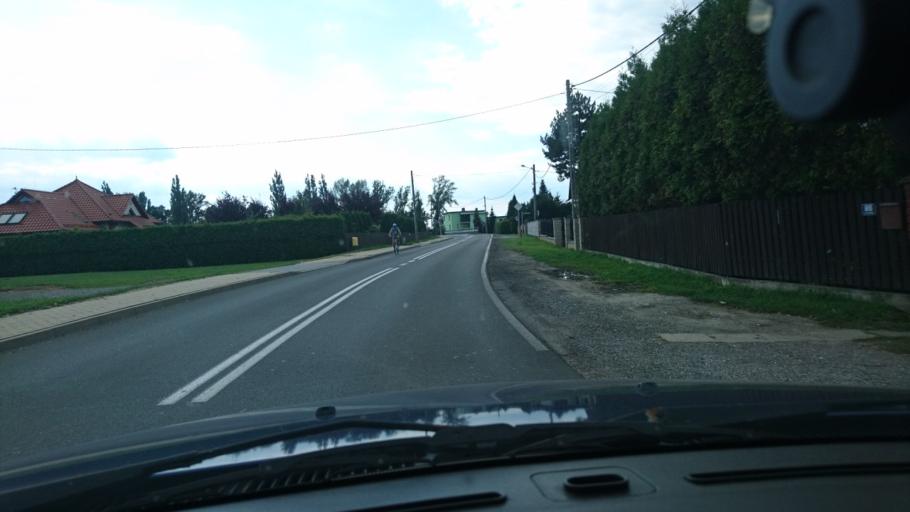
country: PL
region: Silesian Voivodeship
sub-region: Powiat bielski
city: Ligota
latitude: 49.8988
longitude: 18.9529
